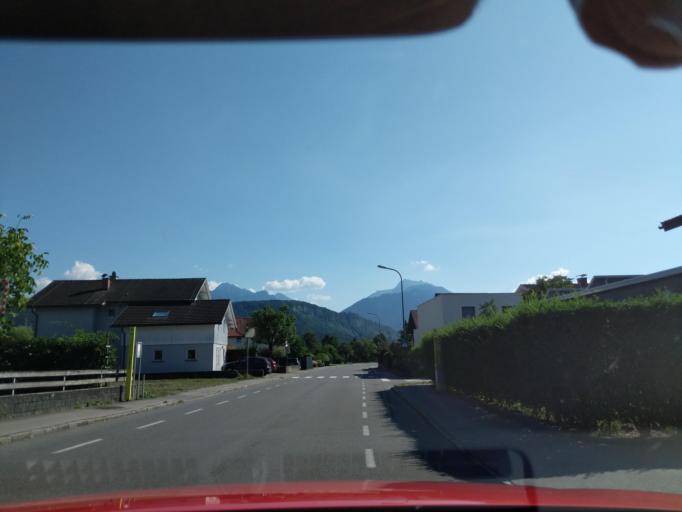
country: AT
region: Vorarlberg
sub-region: Politischer Bezirk Feldkirch
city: Rankweil
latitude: 47.2748
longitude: 9.6306
